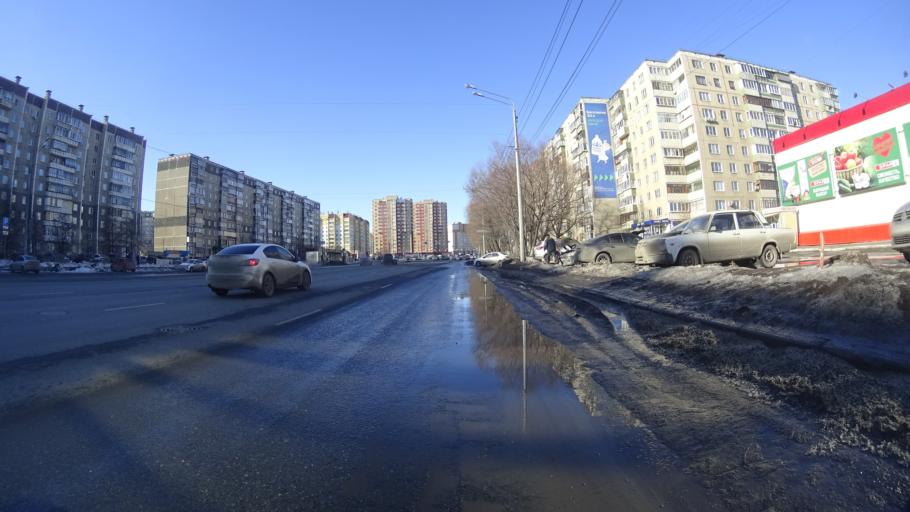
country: RU
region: Chelyabinsk
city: Roshchino
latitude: 55.1895
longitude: 61.2832
